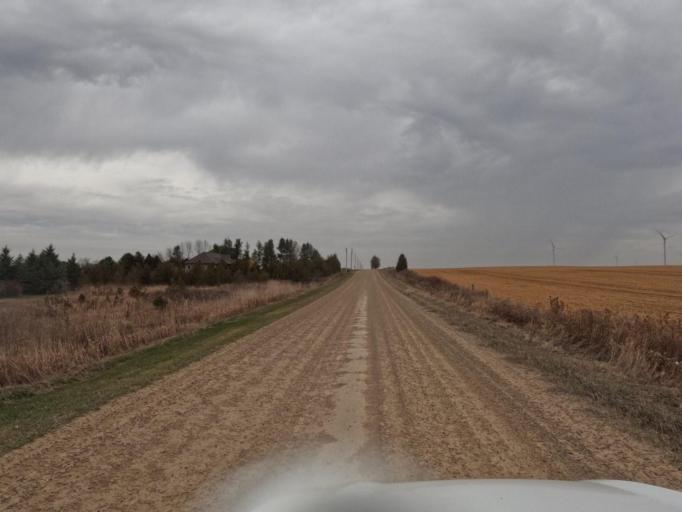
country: CA
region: Ontario
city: Shelburne
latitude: 43.8774
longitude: -80.3802
